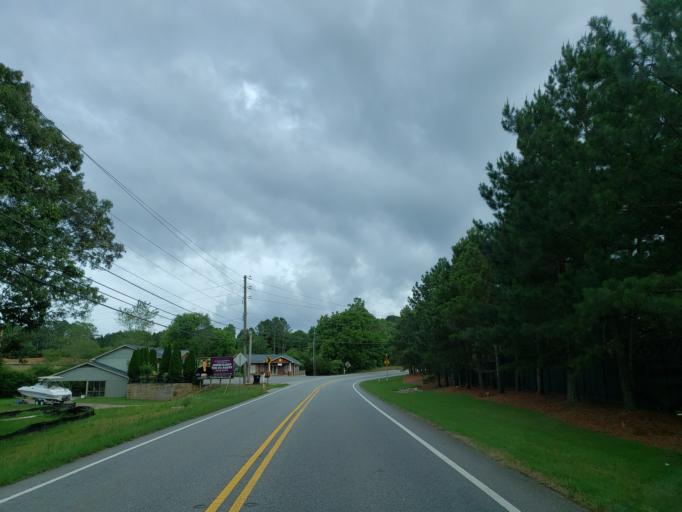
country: US
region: Georgia
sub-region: Cherokee County
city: Ball Ground
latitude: 34.2423
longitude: -84.3526
